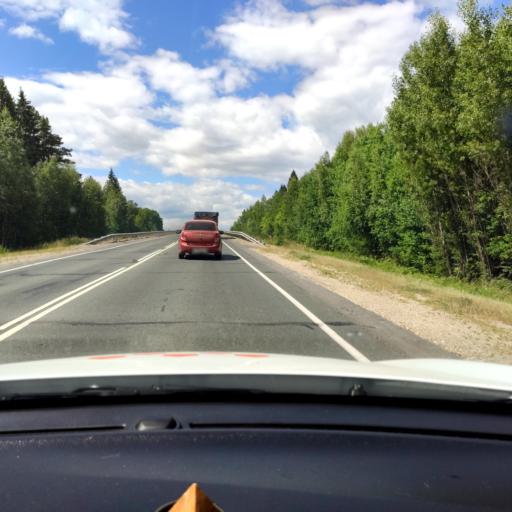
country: RU
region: Mariy-El
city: Volzhsk
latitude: 55.9052
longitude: 48.3785
